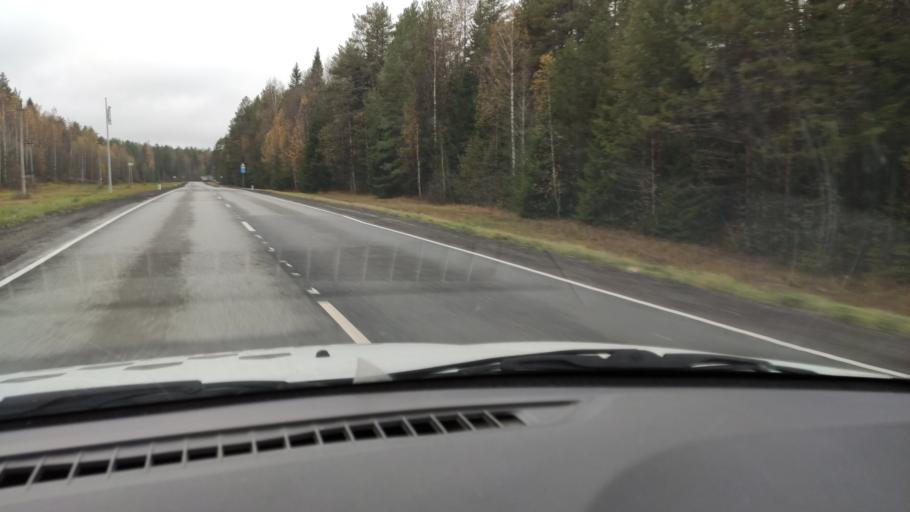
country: RU
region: Kirov
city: Belaya Kholunitsa
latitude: 58.8305
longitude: 50.6826
